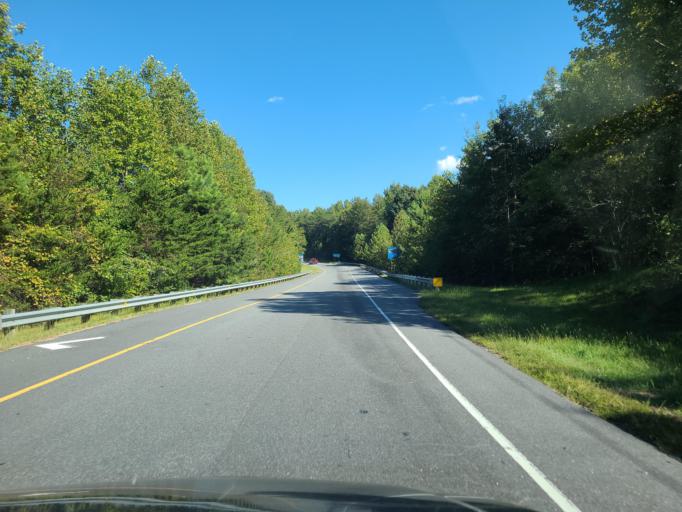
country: US
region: North Carolina
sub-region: Catawba County
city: Conover
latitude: 35.7217
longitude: -81.2080
